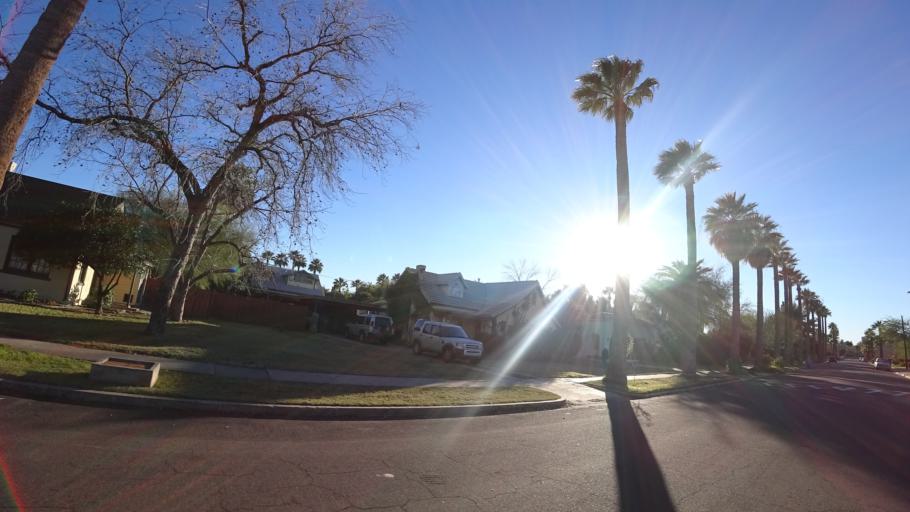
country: US
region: Arizona
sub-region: Maricopa County
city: Phoenix
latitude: 33.4854
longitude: -112.0497
